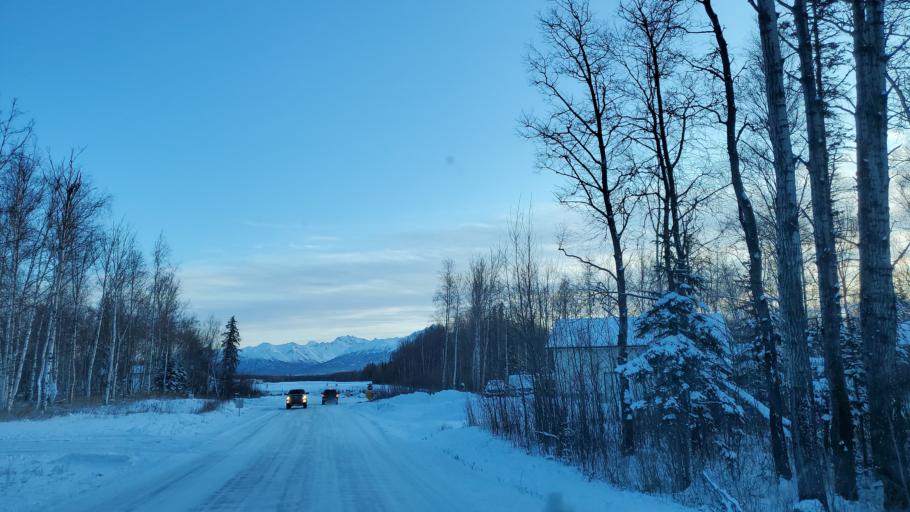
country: US
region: Alaska
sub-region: Matanuska-Susitna Borough
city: Lakes
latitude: 61.6393
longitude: -149.3073
